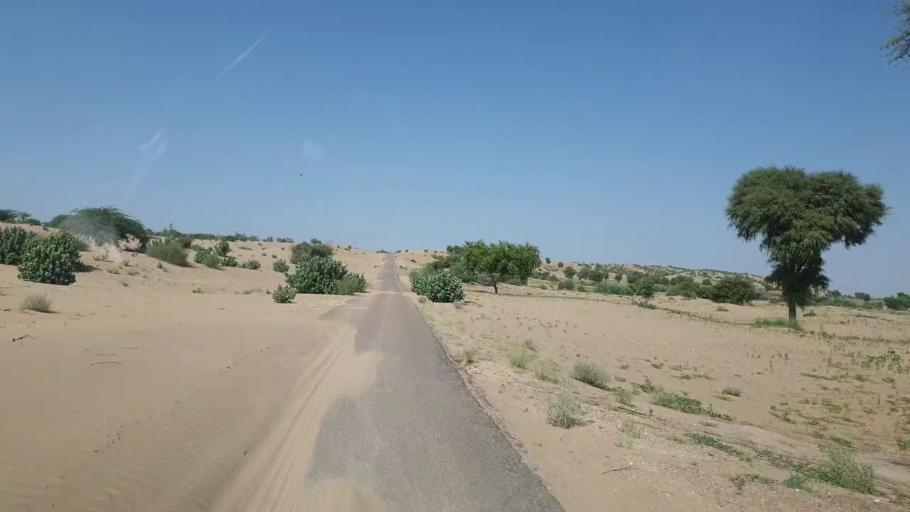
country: PK
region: Sindh
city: Chor
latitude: 25.6115
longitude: 70.3168
